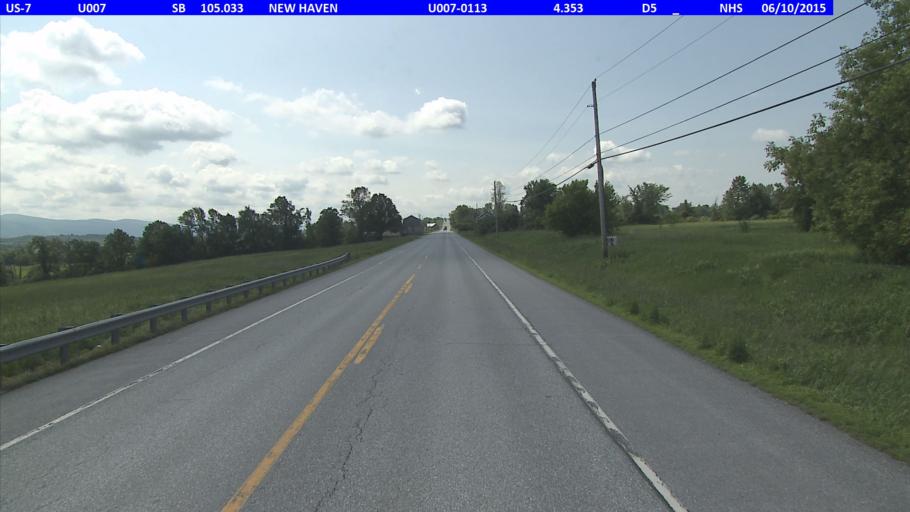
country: US
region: Vermont
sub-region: Addison County
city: Middlebury (village)
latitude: 44.1090
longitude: -73.1747
